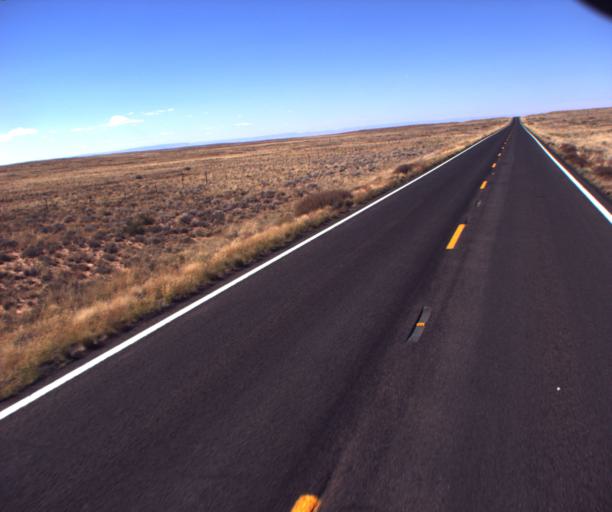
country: US
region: Arizona
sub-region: Coconino County
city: Tuba City
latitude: 35.9662
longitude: -110.9523
